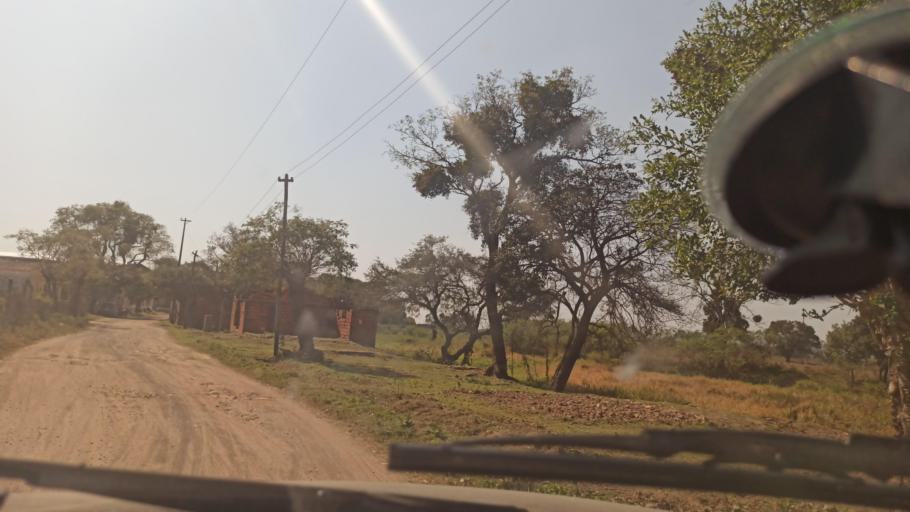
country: AR
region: Formosa
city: Clorinda
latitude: -25.3142
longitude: -57.6985
